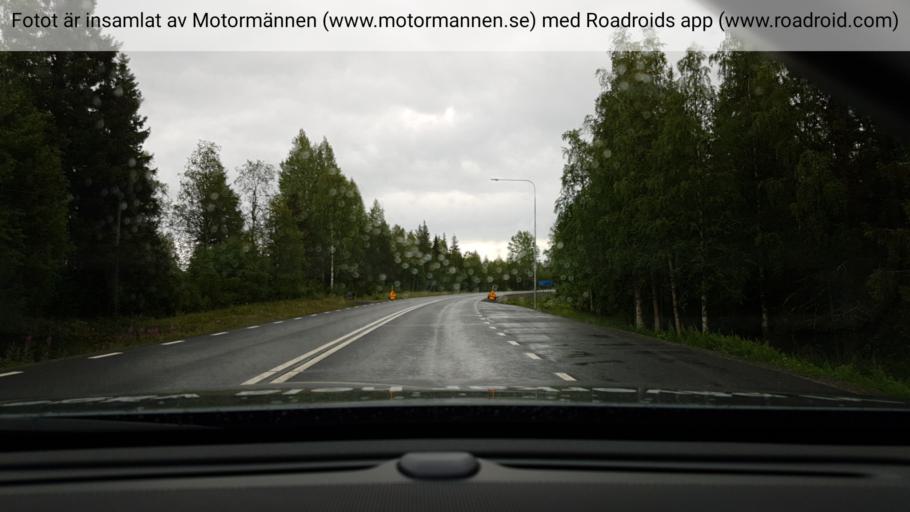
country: SE
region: Vaesterbotten
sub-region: Norsjo Kommun
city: Norsjoe
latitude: 65.2620
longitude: 19.6588
